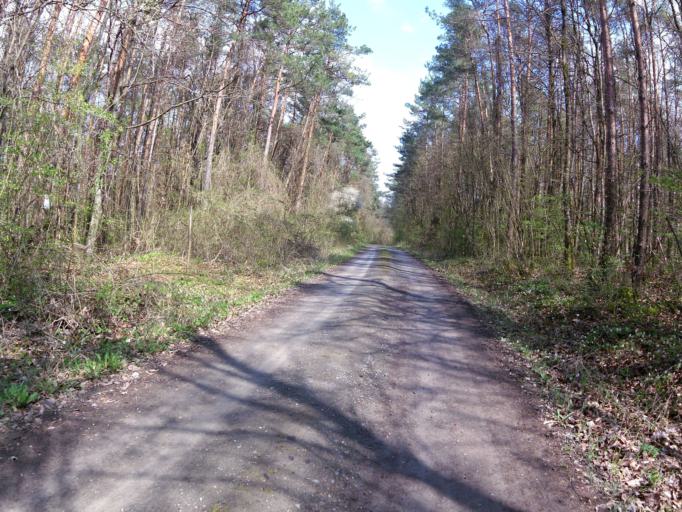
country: DE
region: Bavaria
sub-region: Regierungsbezirk Unterfranken
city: Rimpar
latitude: 49.8676
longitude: 9.9393
